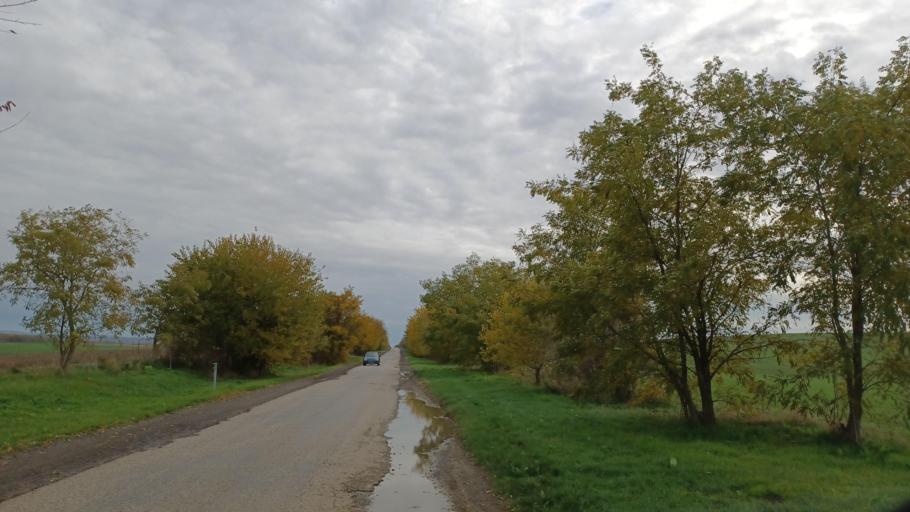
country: HU
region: Tolna
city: Simontornya
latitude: 46.7012
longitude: 18.5864
